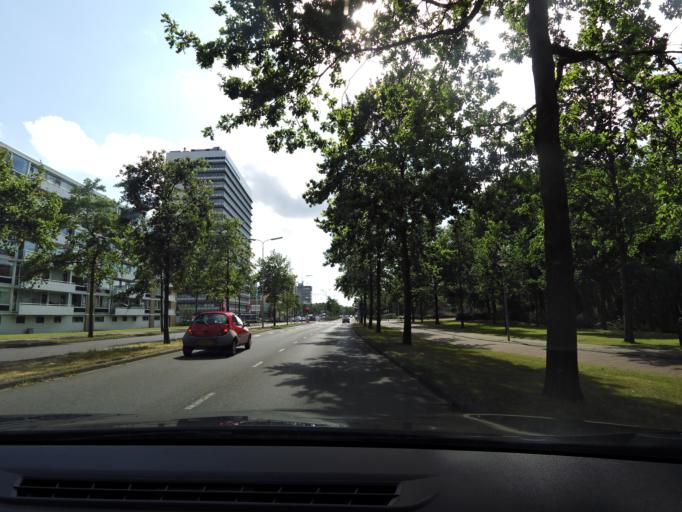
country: NL
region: South Holland
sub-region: Gemeente Rijswijk
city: Rijswijk
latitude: 52.0400
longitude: 4.3158
